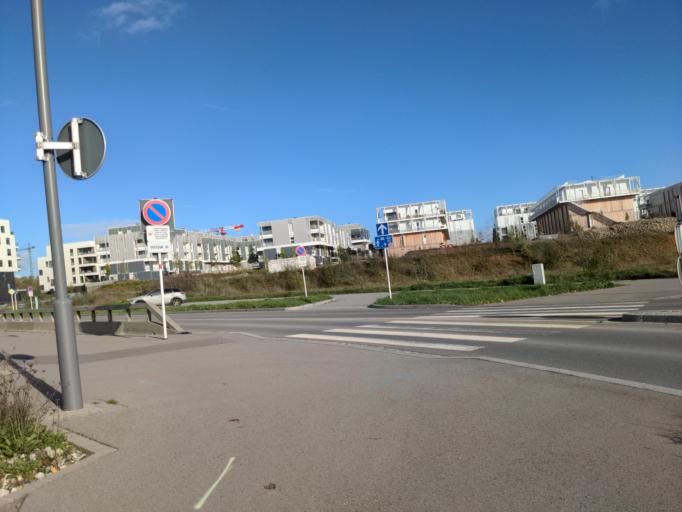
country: LU
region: Luxembourg
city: Kirchberg
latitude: 49.6338
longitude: 6.1585
